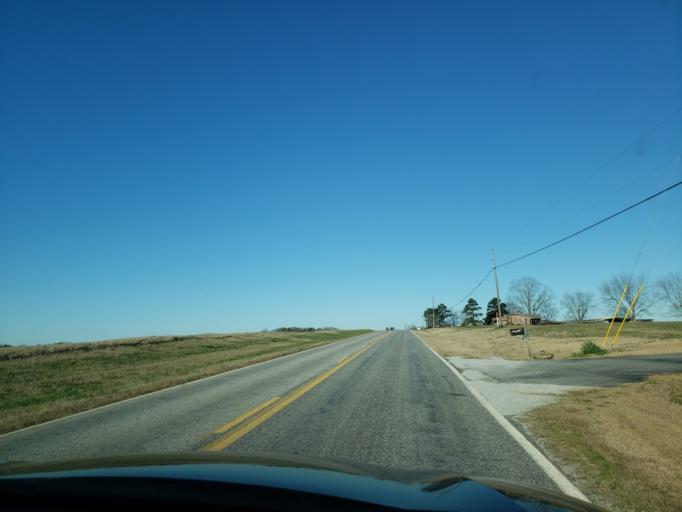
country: US
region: Alabama
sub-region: Elmore County
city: Tallassee
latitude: 32.5813
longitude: -85.7778
